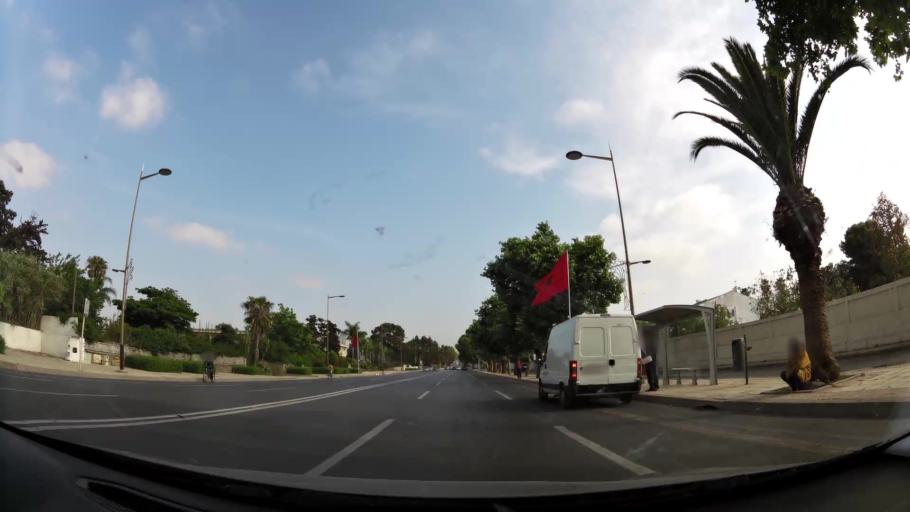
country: MA
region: Rabat-Sale-Zemmour-Zaer
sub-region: Rabat
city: Rabat
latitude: 33.9621
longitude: -6.8268
